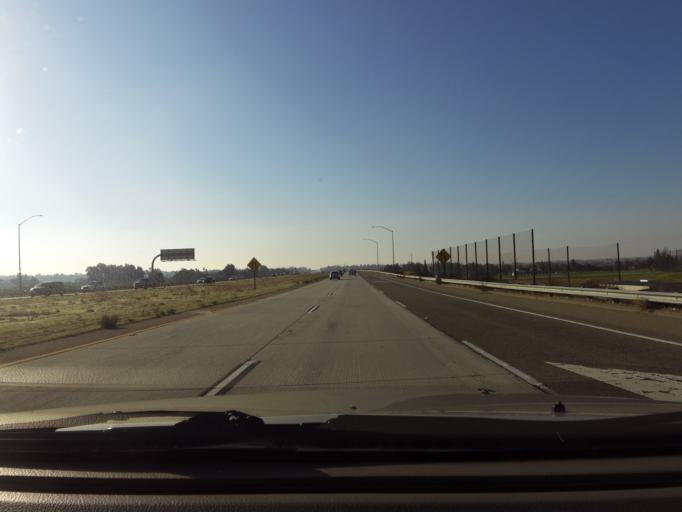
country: US
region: California
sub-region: Fresno County
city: Clovis
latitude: 36.8847
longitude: -119.7937
